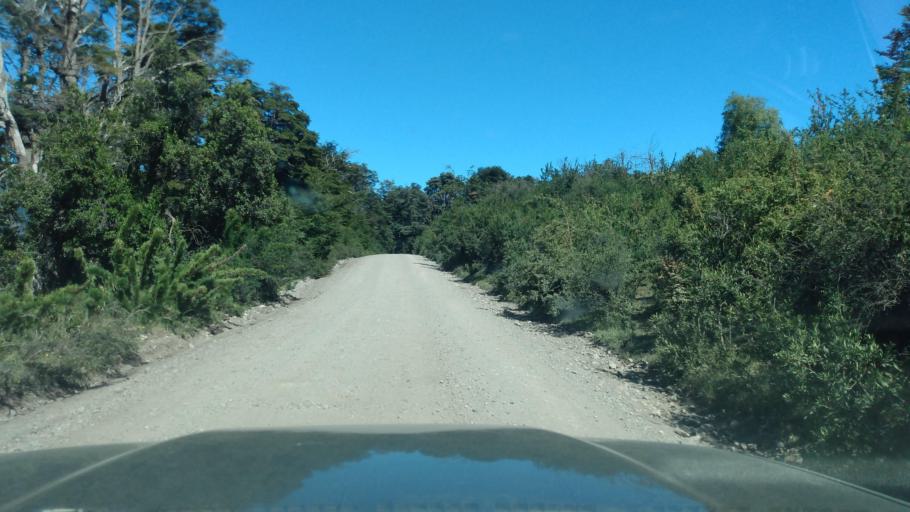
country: AR
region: Neuquen
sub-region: Departamento de Lacar
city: San Martin de los Andes
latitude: -39.7508
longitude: -71.4580
